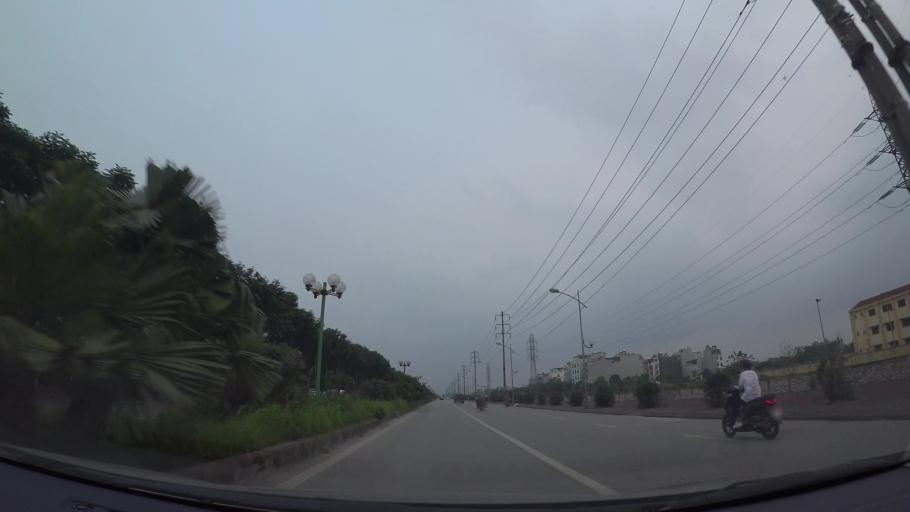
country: VN
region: Ha Noi
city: Trau Quy
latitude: 21.0609
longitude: 105.9021
